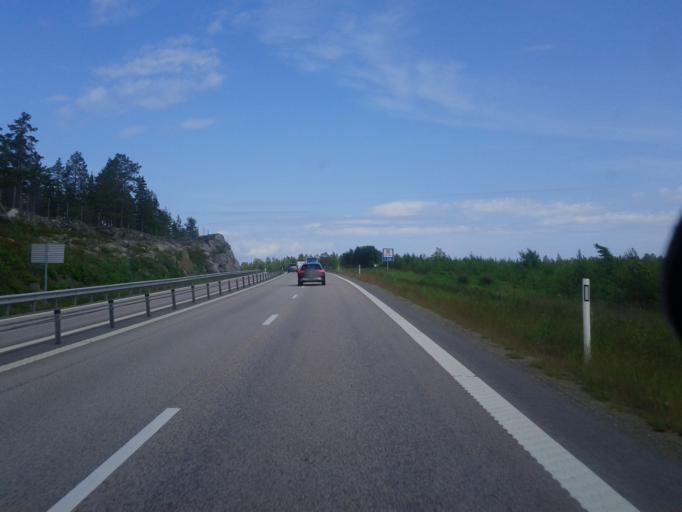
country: SE
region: Vaesternorrland
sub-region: OErnskoeldsviks Kommun
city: Husum
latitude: 63.3661
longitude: 19.1844
